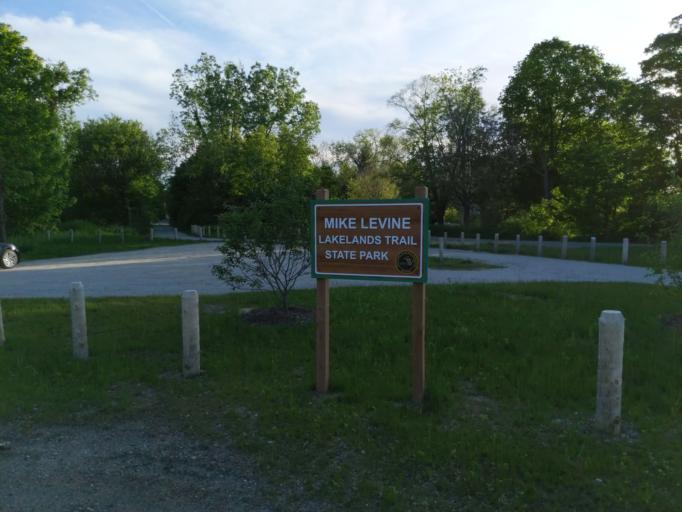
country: US
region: Michigan
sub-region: Ingham County
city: Stockbridge
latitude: 42.3907
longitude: -84.2506
